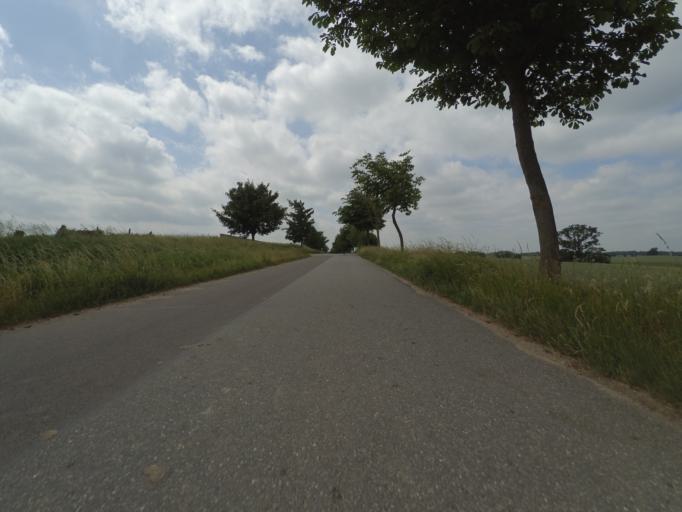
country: DE
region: Mecklenburg-Vorpommern
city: Klink
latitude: 53.4744
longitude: 12.6006
